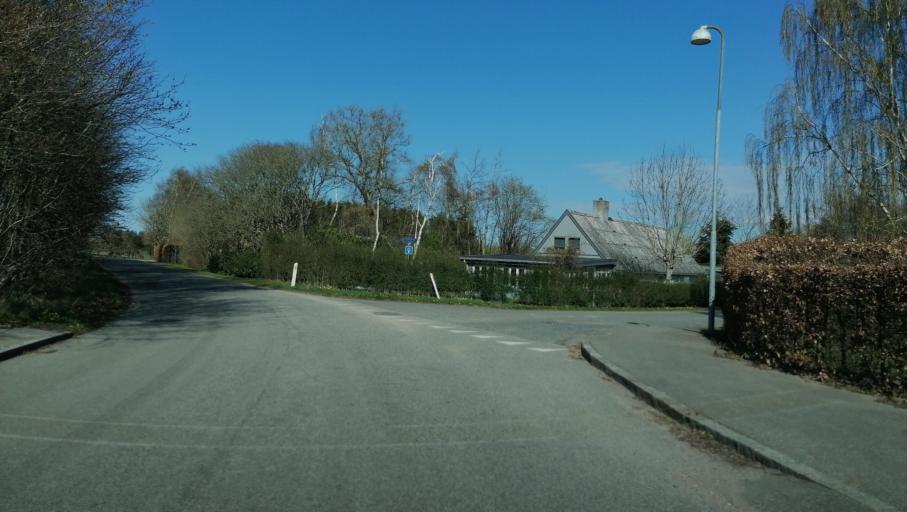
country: DK
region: Zealand
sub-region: Holbaek Kommune
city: Jyderup
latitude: 55.7212
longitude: 11.3867
